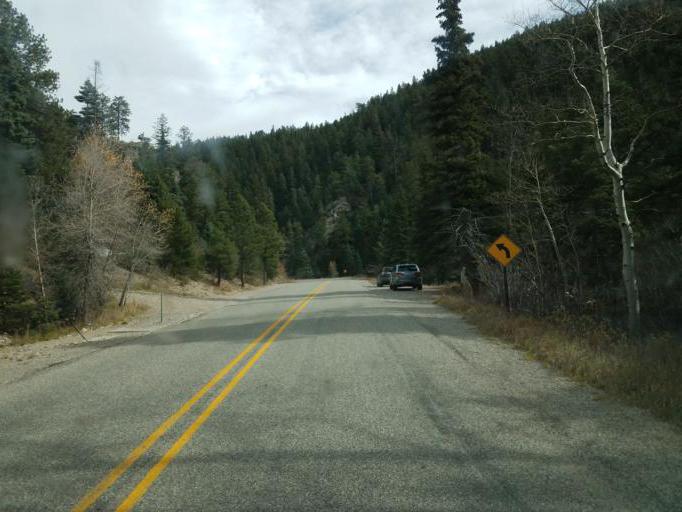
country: US
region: New Mexico
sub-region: Taos County
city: Arroyo Seco
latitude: 36.5691
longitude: -105.5189
